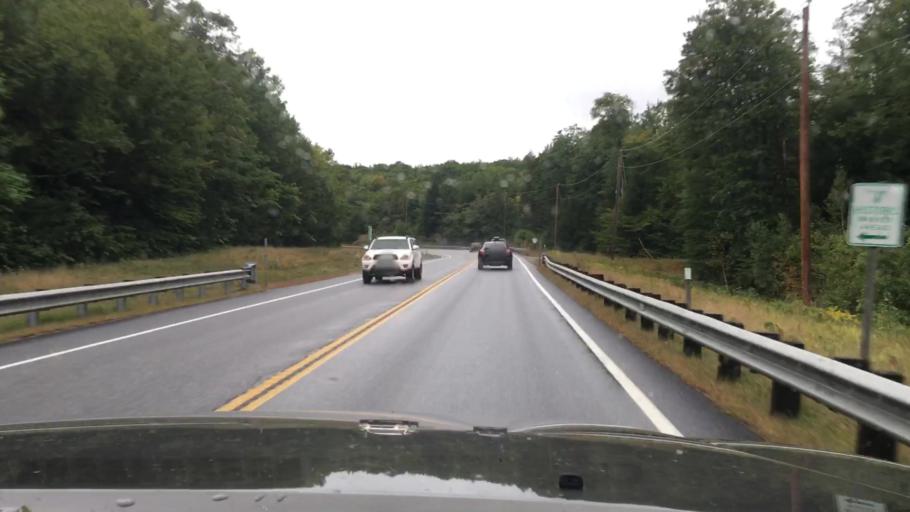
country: US
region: New Hampshire
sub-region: Hillsborough County
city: Antrim
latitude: 43.0747
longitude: -72.0432
